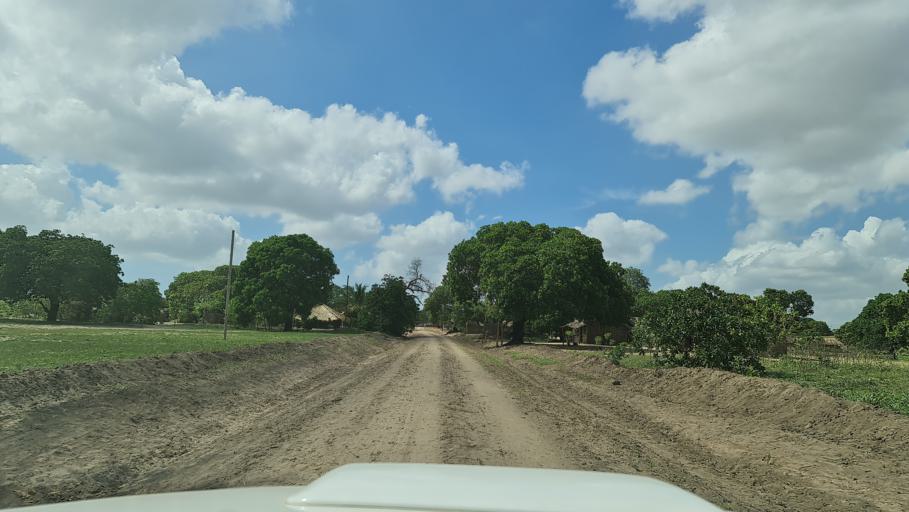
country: MZ
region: Nampula
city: Ilha de Mocambique
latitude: -15.0155
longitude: 40.5601
